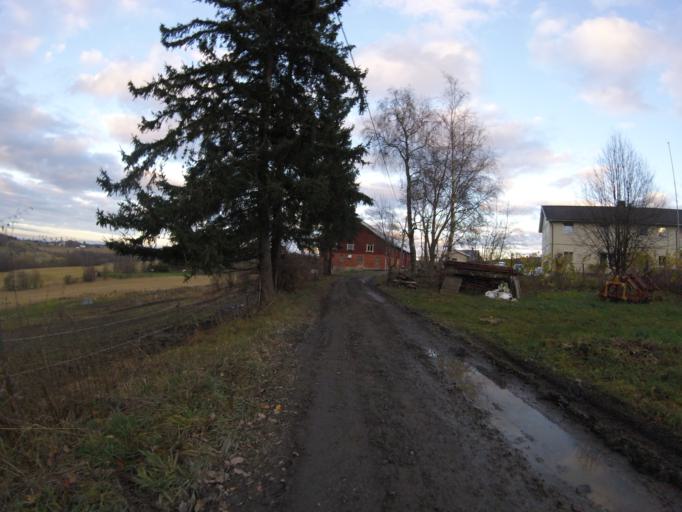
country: NO
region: Akershus
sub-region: Skedsmo
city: Leirsund
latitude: 60.0005
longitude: 11.0969
